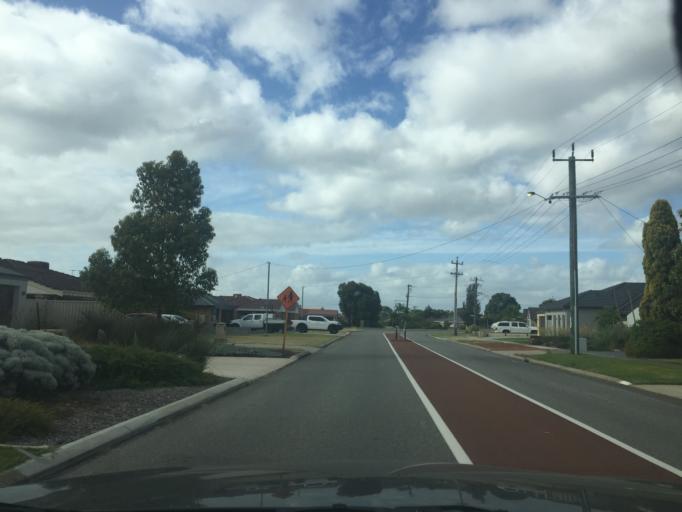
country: AU
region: Western Australia
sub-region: Canning
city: Canning Vale
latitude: -32.0448
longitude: 115.9099
